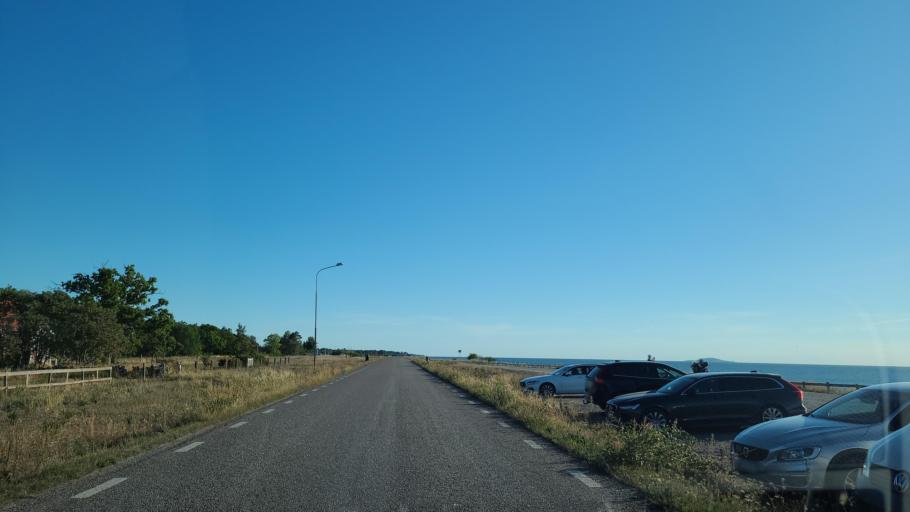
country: SE
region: Kalmar
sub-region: Vasterviks Kommun
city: Vaestervik
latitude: 57.3354
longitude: 17.0119
